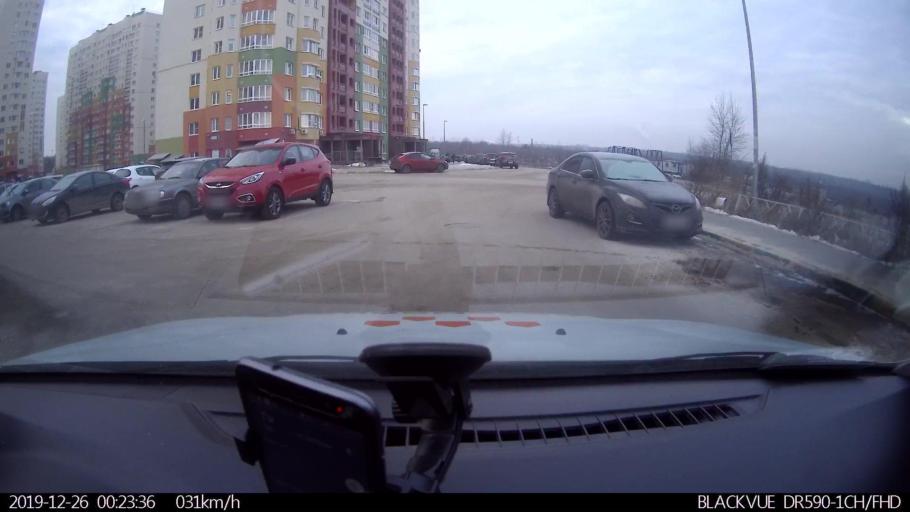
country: RU
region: Nizjnij Novgorod
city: Nizhniy Novgorod
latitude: 56.2661
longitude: 44.0140
